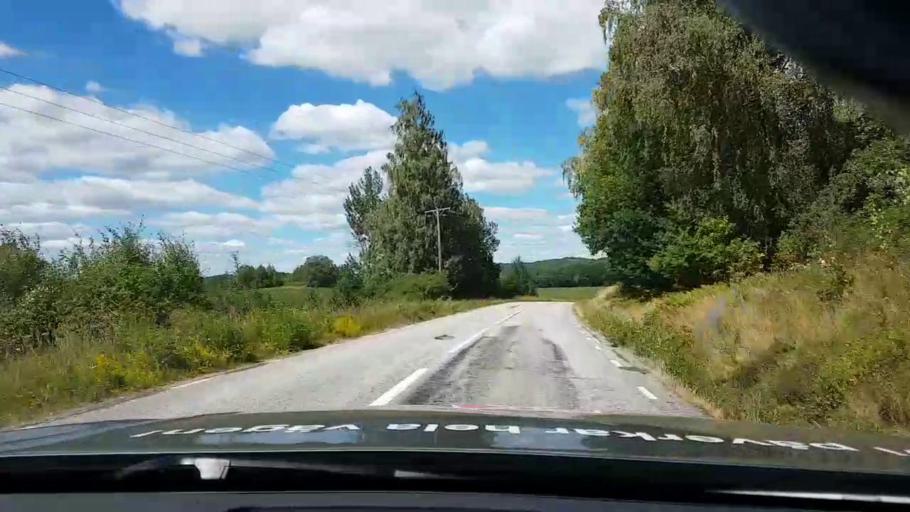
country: SE
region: Kalmar
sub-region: Vasterviks Kommun
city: Overum
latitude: 58.0500
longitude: 16.4072
